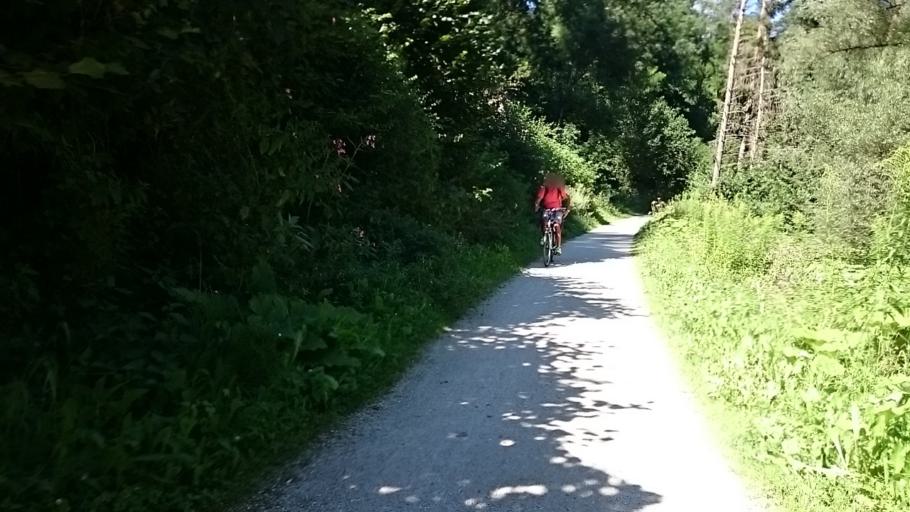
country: IT
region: Trentino-Alto Adige
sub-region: Bolzano
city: Riscone
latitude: 46.7861
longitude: 11.9662
